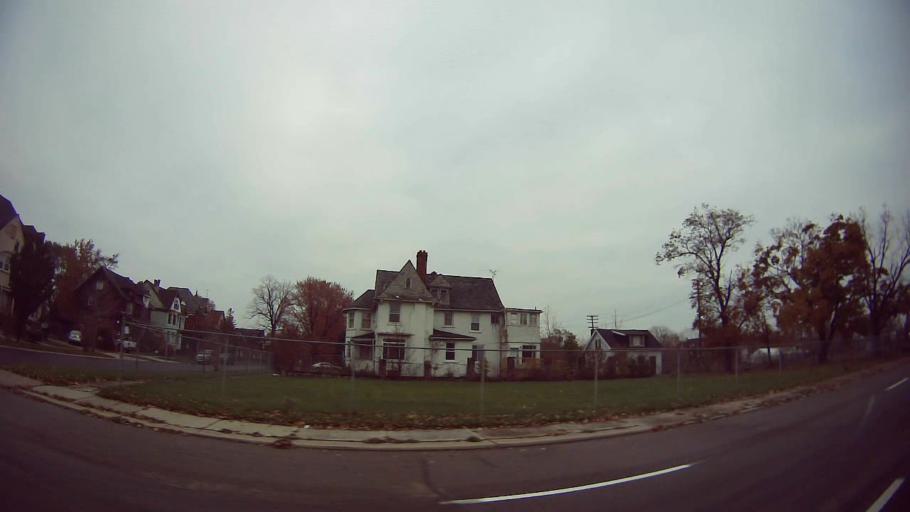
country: US
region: Michigan
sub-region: Wayne County
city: Hamtramck
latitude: 42.3747
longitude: -83.0735
